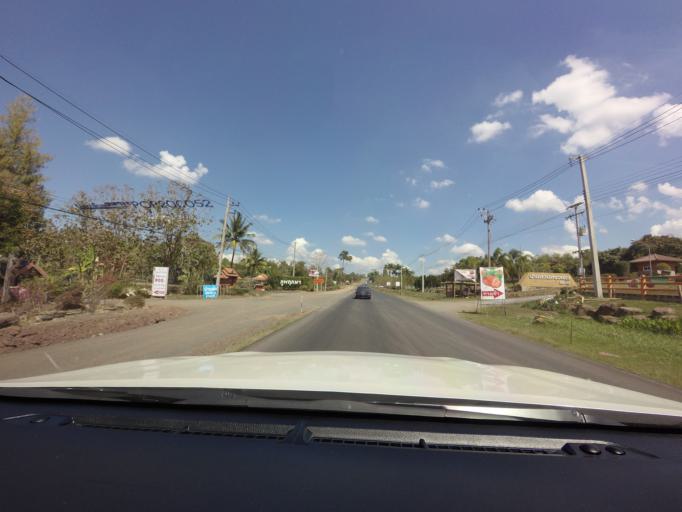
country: TH
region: Nakhon Ratchasima
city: Wang Nam Khiao
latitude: 14.3657
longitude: 101.8956
